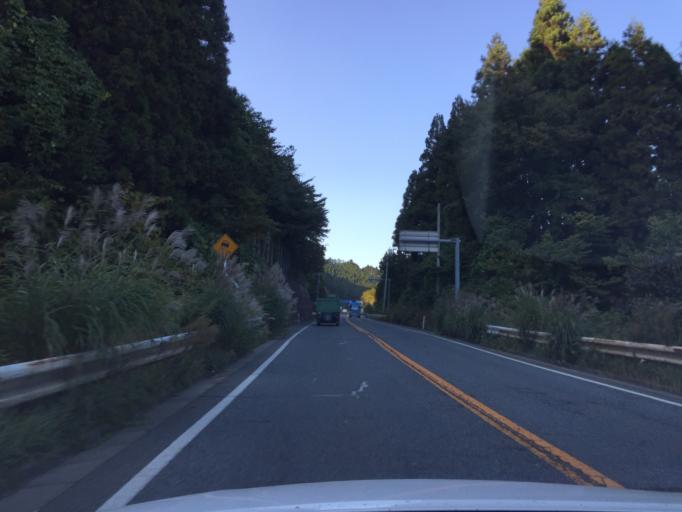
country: JP
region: Fukushima
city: Ishikawa
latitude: 37.1571
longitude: 140.6578
